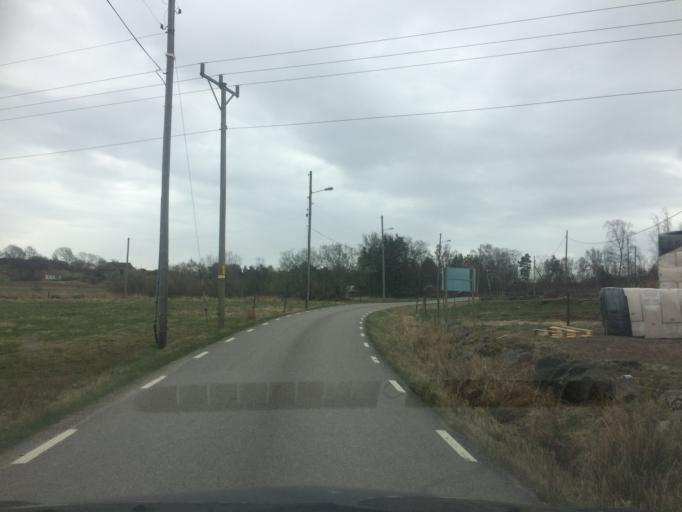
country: SE
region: Vaestra Goetaland
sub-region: Goteborg
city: Majorna
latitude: 57.8048
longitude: 11.8816
